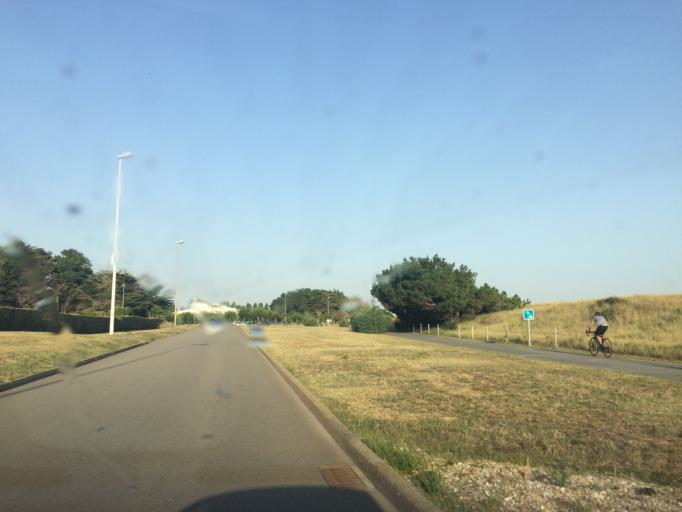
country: FR
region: Brittany
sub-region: Departement du Morbihan
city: Damgan
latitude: 47.5167
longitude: -2.5702
